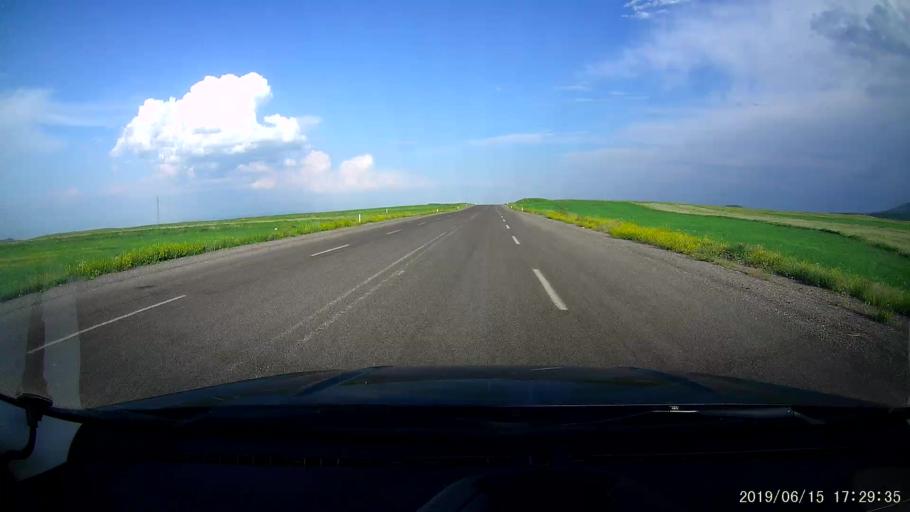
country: TR
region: Kars
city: Basgedikler
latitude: 40.5885
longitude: 43.4547
